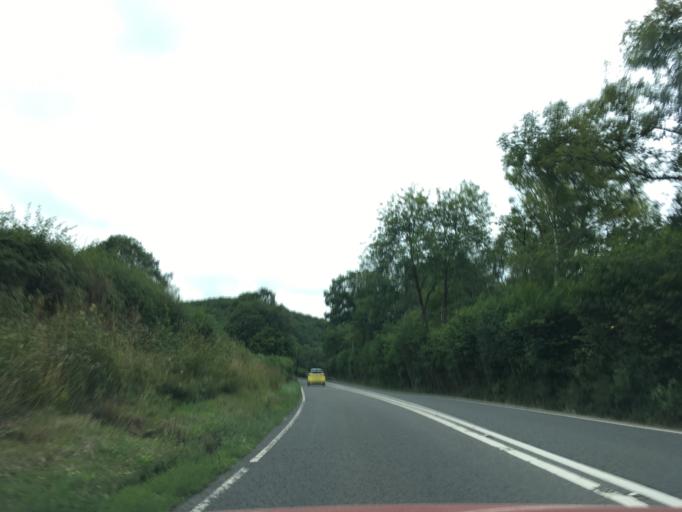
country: GB
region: Wales
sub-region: Carmarthenshire
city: Llandovery
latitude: 51.9889
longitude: -3.7265
